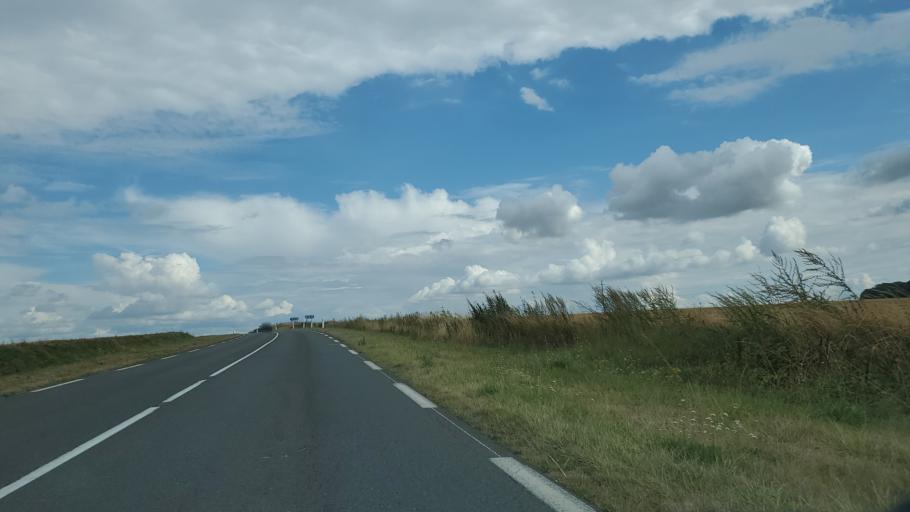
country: FR
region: Ile-de-France
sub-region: Departement de Seine-et-Marne
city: Chailly-en-Brie
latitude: 48.7877
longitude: 3.1307
